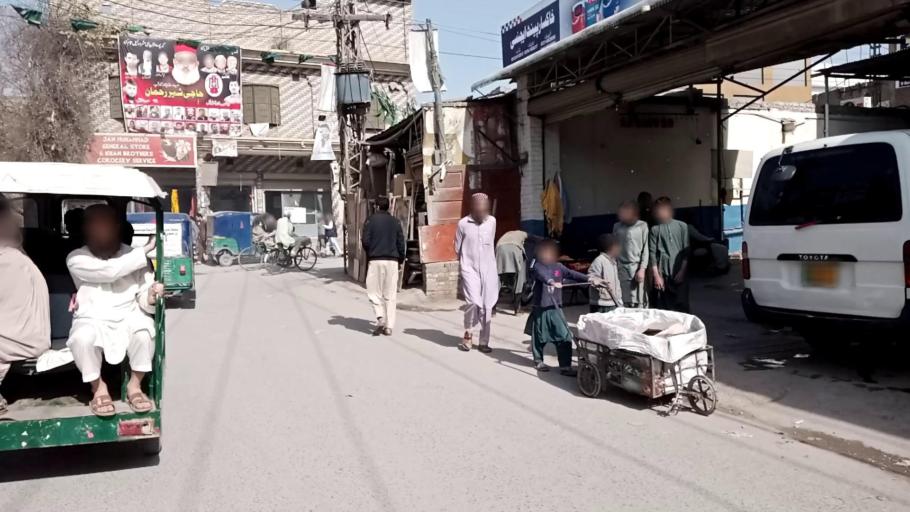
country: PK
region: Khyber Pakhtunkhwa
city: Peshawar
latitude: 33.9955
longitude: 71.5782
